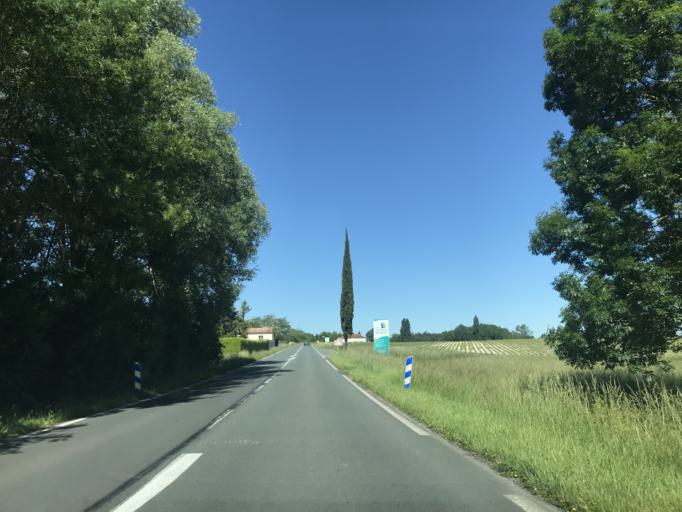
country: FR
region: Poitou-Charentes
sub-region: Departement de la Charente
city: Barbezieux-Saint-Hilaire
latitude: 45.4981
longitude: -0.2451
